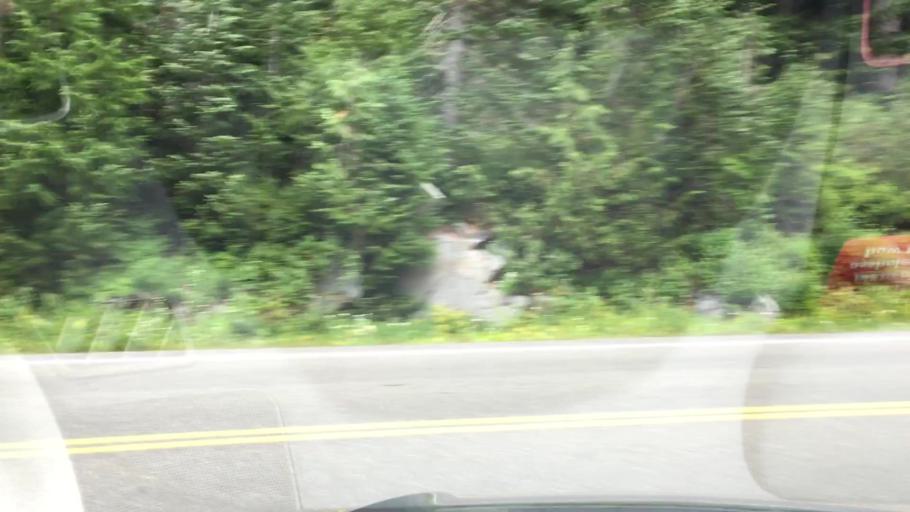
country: US
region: Washington
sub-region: Pierce County
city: Buckley
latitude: 46.7788
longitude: -121.7393
